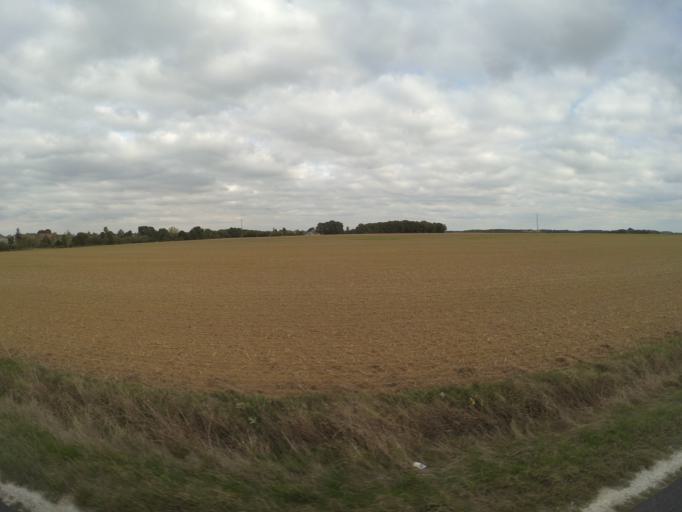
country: FR
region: Centre
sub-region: Departement d'Indre-et-Loire
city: Nazelles-Negron
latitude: 47.4831
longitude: 0.9491
